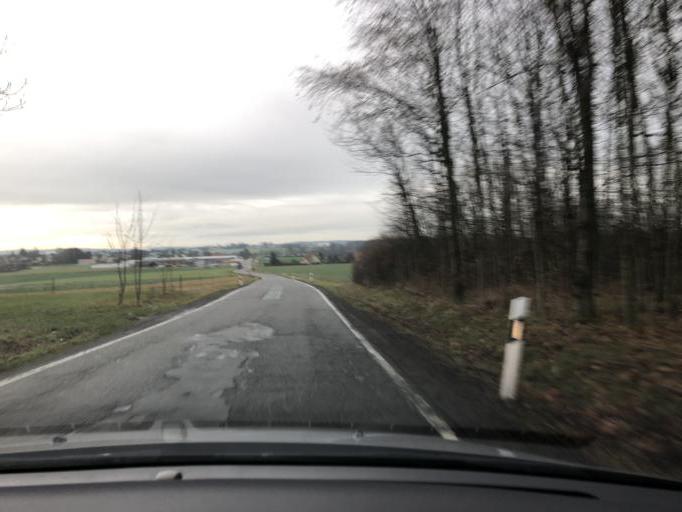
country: DE
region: Saxony
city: Niederfrohna
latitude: 50.8702
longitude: 12.7283
